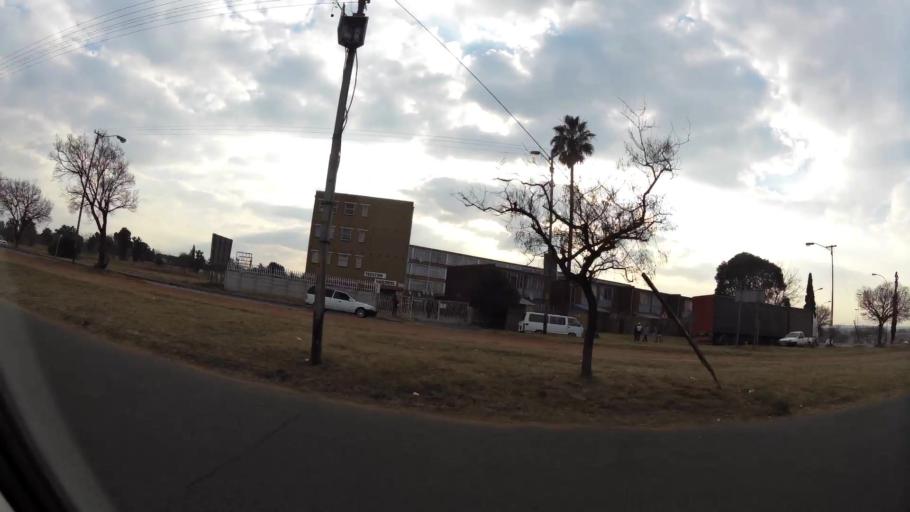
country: ZA
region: Gauteng
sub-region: Ekurhuleni Metropolitan Municipality
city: Germiston
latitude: -26.2386
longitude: 28.1959
